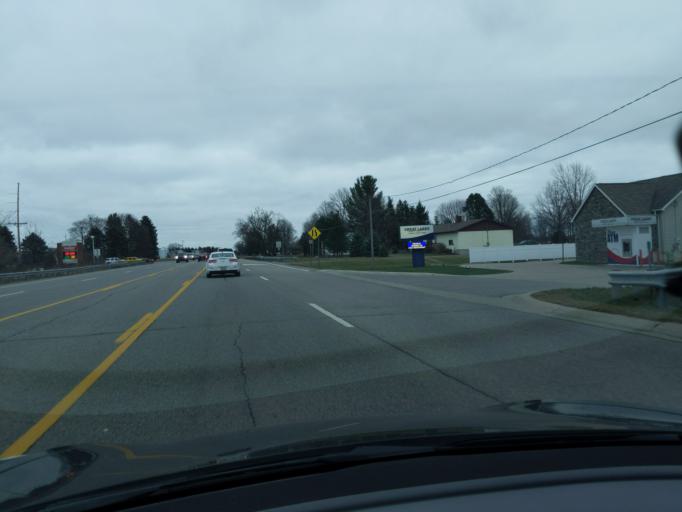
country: US
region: Michigan
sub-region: Saginaw County
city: Birch Run
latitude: 43.2502
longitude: -83.7667
